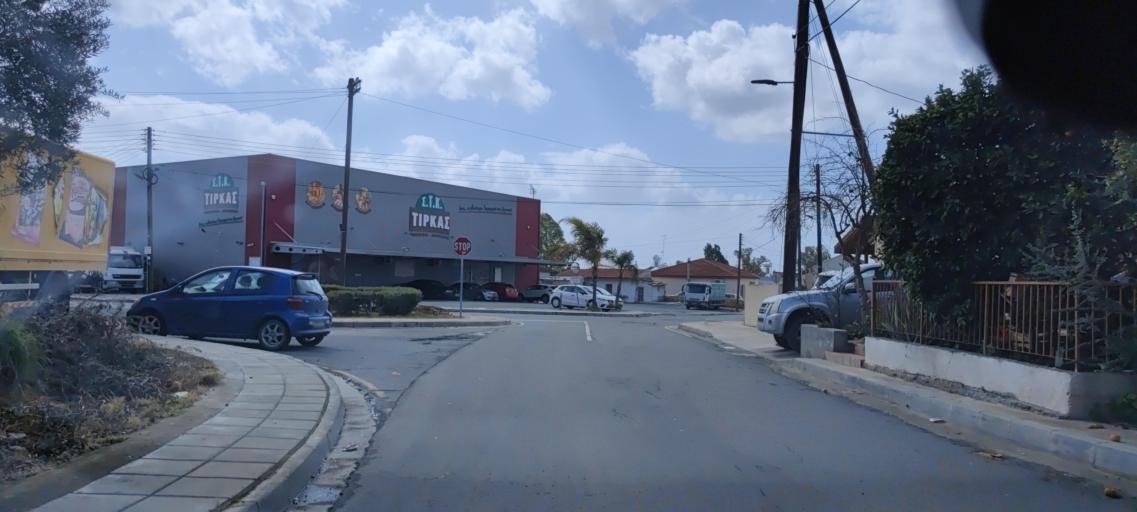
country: CY
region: Limassol
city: Pano Polemidia
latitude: 34.6928
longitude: 32.9955
